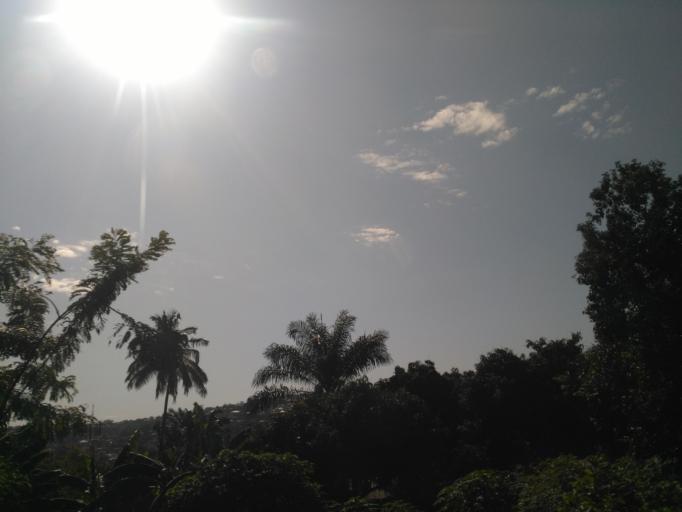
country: TZ
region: Mwanza
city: Mwanza
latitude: -2.4978
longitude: 32.8977
